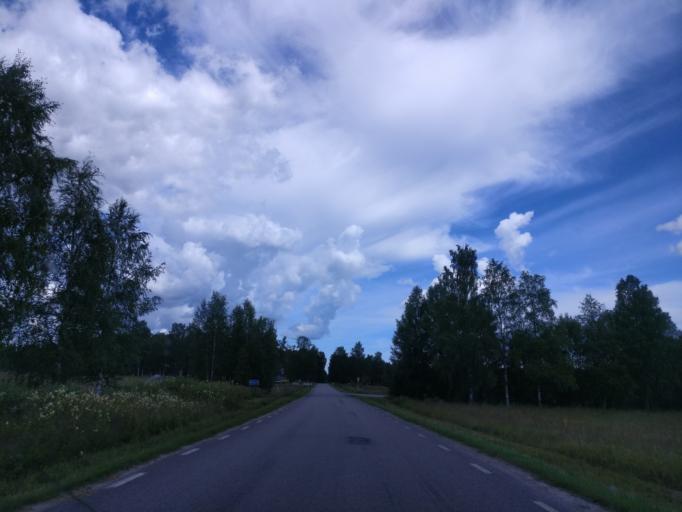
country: SE
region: Vaermland
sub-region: Hagfors Kommun
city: Ekshaerad
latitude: 60.1294
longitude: 13.4577
